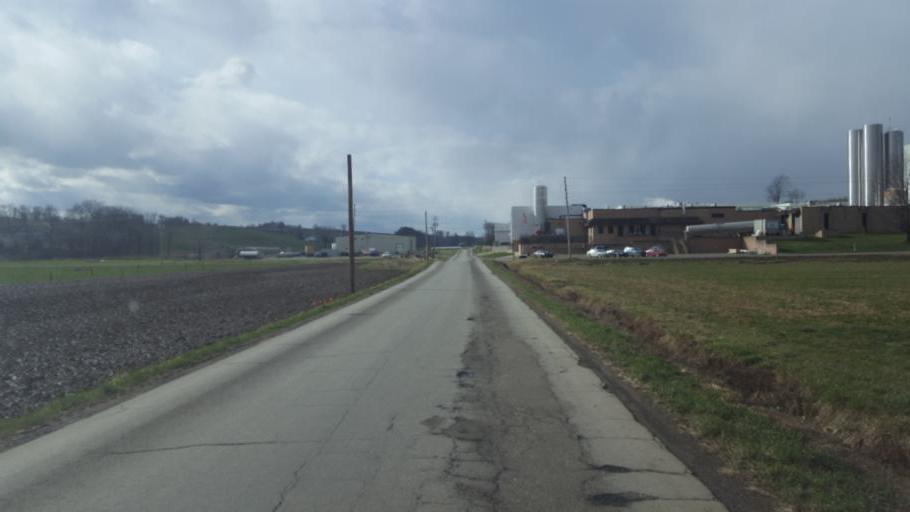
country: US
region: Ohio
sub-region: Tuscarawas County
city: Sugarcreek
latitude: 40.4905
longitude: -81.6800
